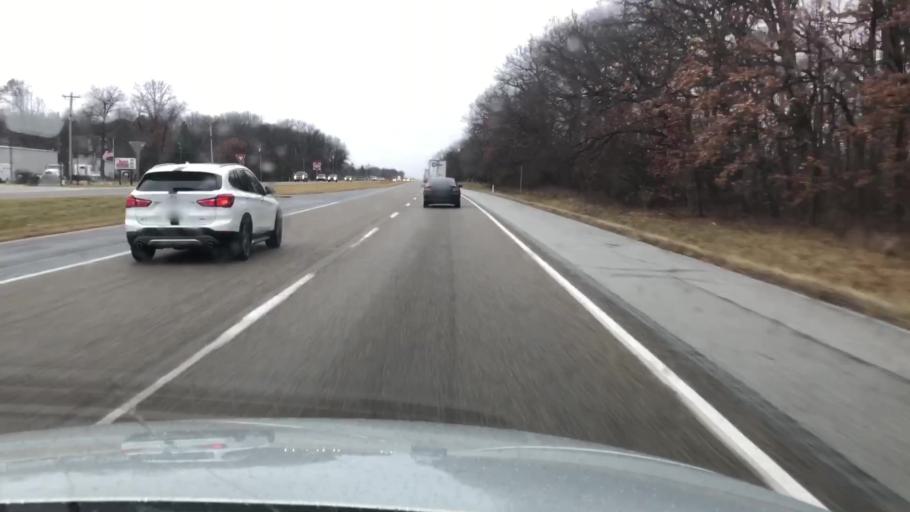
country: US
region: Indiana
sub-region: LaPorte County
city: Wanatah
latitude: 41.4337
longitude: -86.8214
